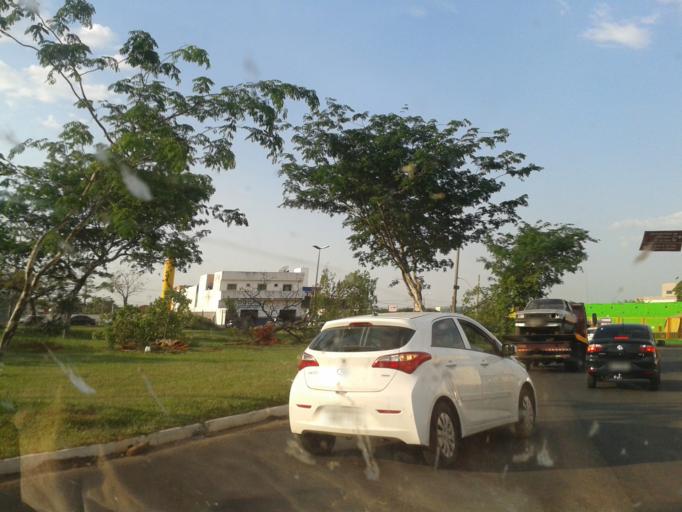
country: BR
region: Minas Gerais
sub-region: Uberlandia
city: Uberlandia
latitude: -18.9394
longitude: -48.3072
